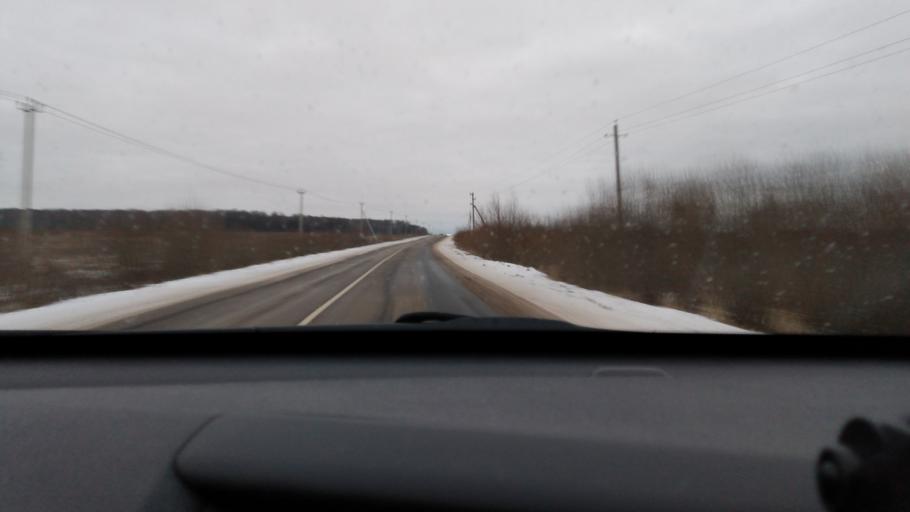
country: RU
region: Moskovskaya
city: Meshcherino
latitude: 55.2909
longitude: 38.2897
